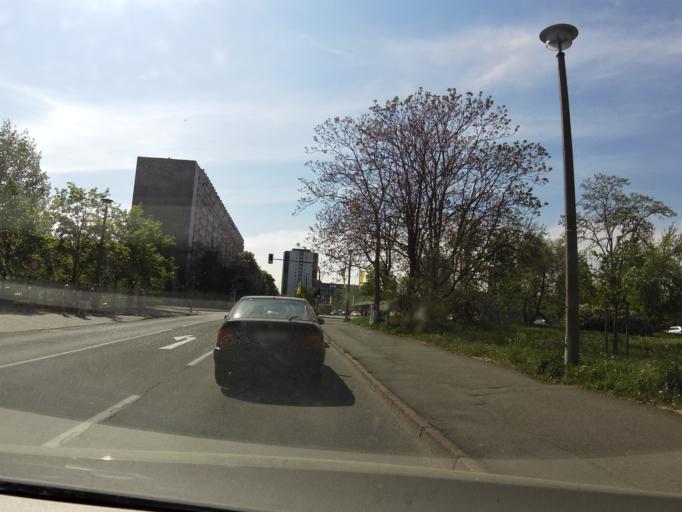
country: DE
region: Thuringia
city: Erfurt
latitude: 51.0110
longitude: 10.9984
